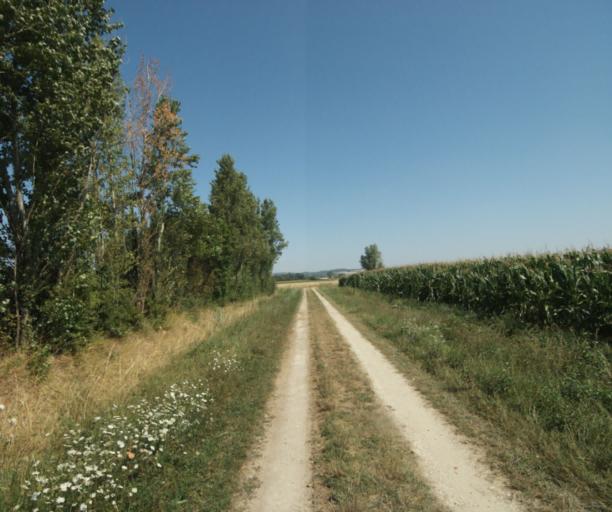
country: FR
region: Midi-Pyrenees
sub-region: Departement de la Haute-Garonne
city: Revel
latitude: 43.5114
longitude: 1.9621
